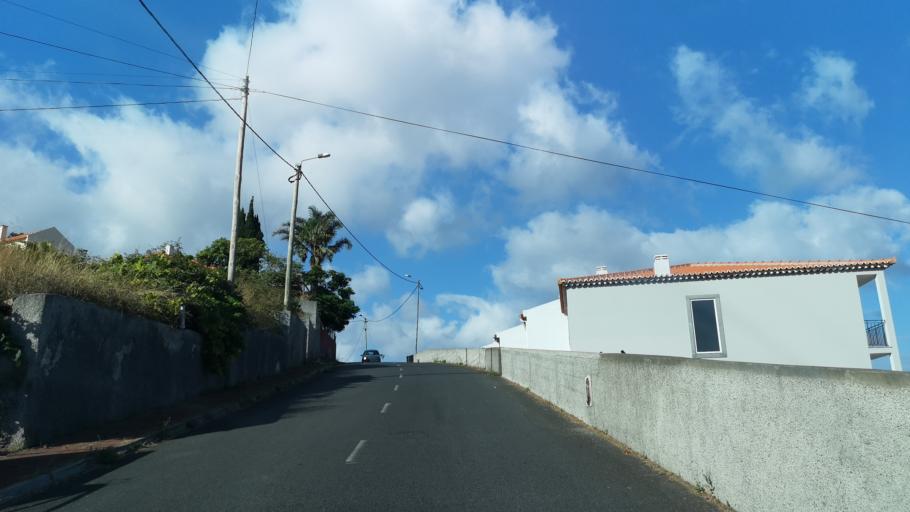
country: PT
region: Madeira
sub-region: Santa Cruz
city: Camacha
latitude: 32.6551
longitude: -16.8348
